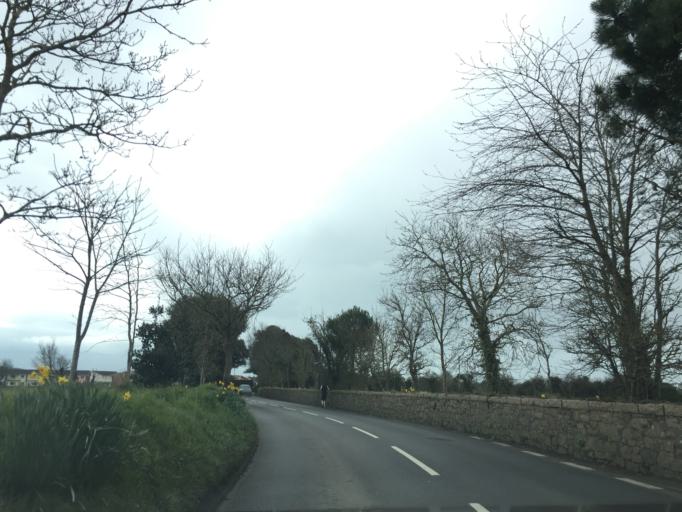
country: JE
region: St Helier
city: Saint Helier
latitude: 49.2123
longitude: -2.1417
